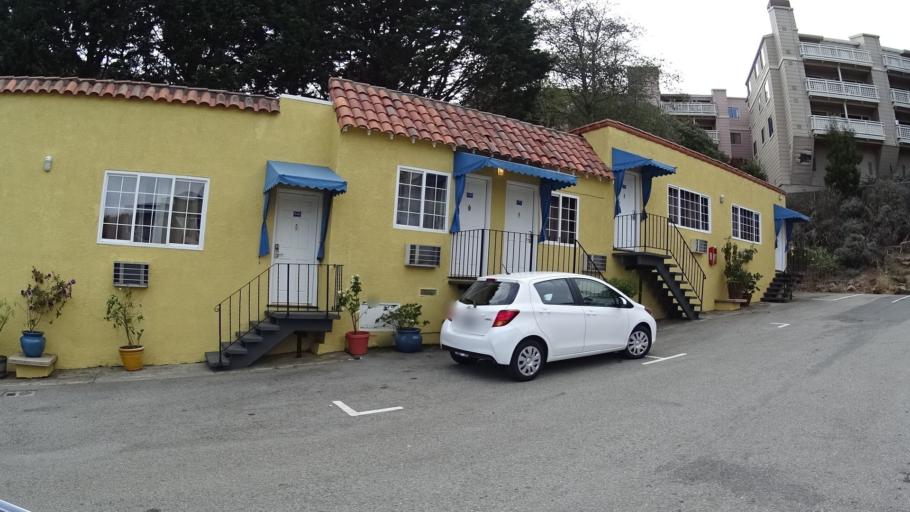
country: US
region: California
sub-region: San Mateo County
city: Daly City
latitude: 37.7084
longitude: -122.4251
